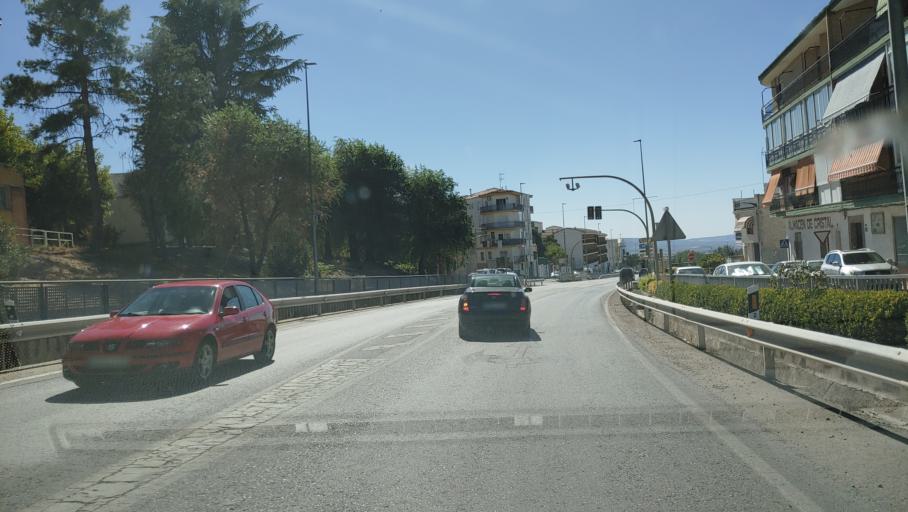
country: ES
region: Andalusia
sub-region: Provincia de Jaen
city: Villacarrillo
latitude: 38.1182
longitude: -3.0821
